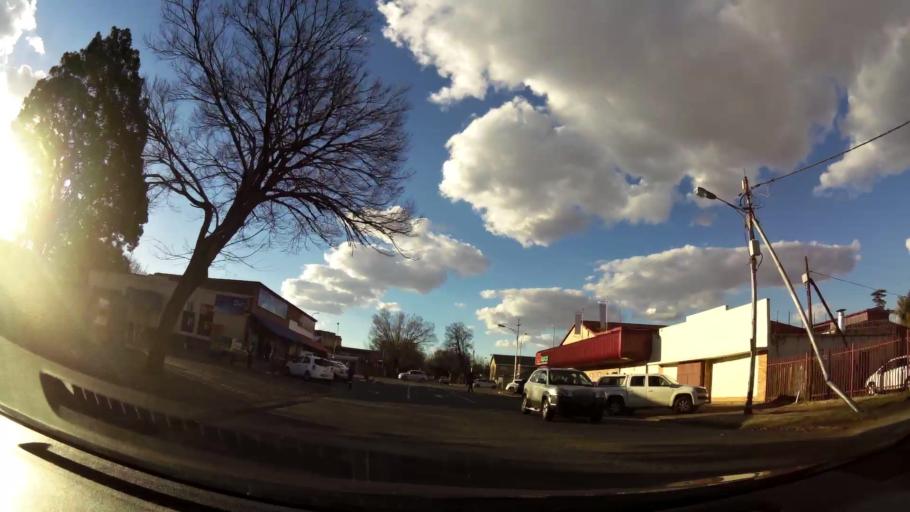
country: ZA
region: North-West
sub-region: Dr Kenneth Kaunda District Municipality
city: Potchefstroom
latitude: -26.7004
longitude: 27.0887
